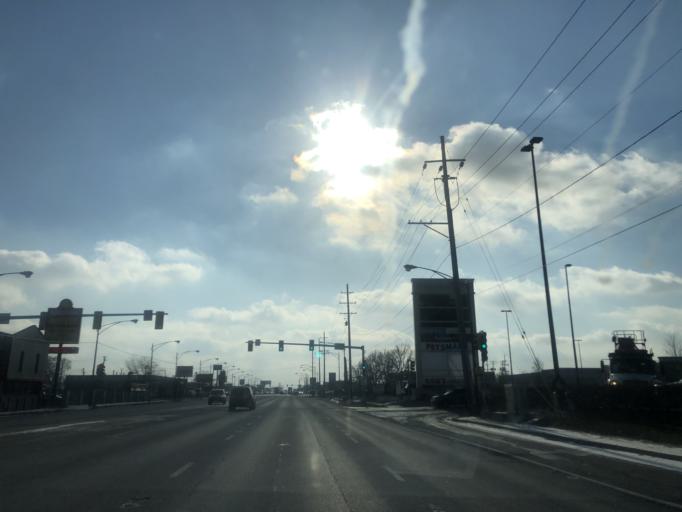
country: US
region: Illinois
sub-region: Cook County
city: Hometown
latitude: 41.7531
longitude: -87.7416
